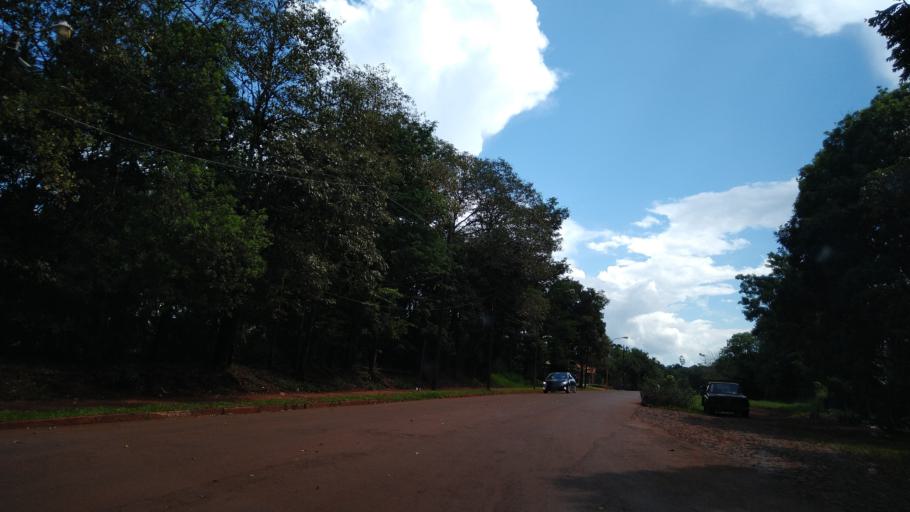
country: AR
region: Misiones
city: Puerto Libertad
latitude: -25.9683
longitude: -54.5848
